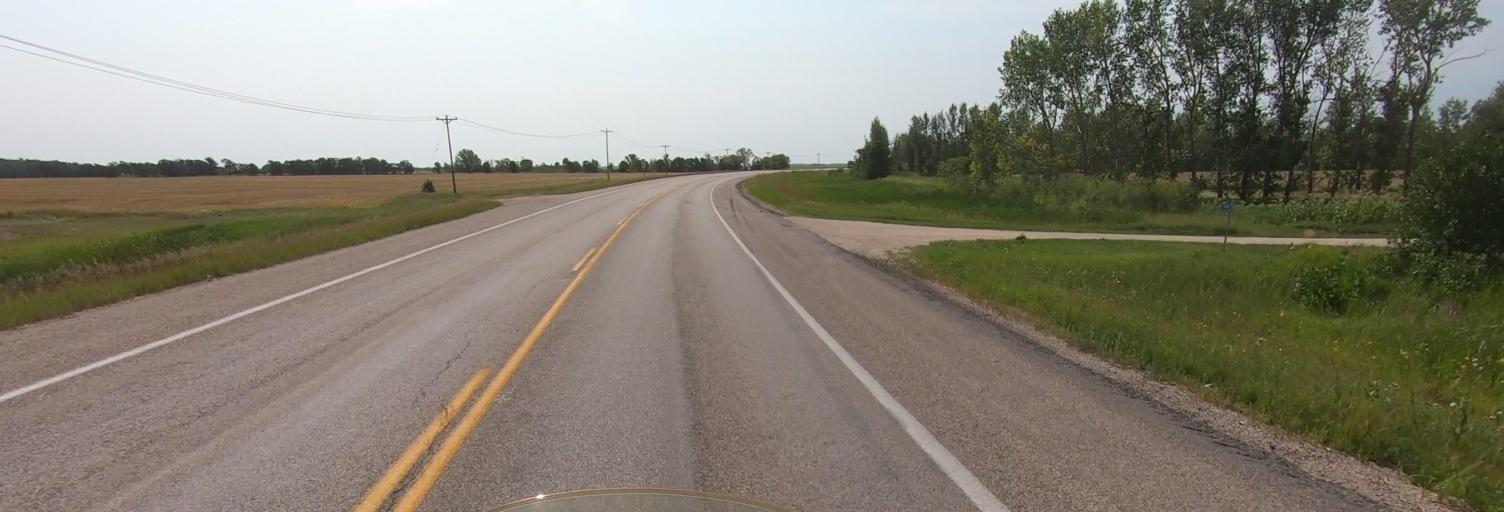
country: CA
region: Manitoba
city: Niverville
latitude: 49.6594
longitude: -97.1021
